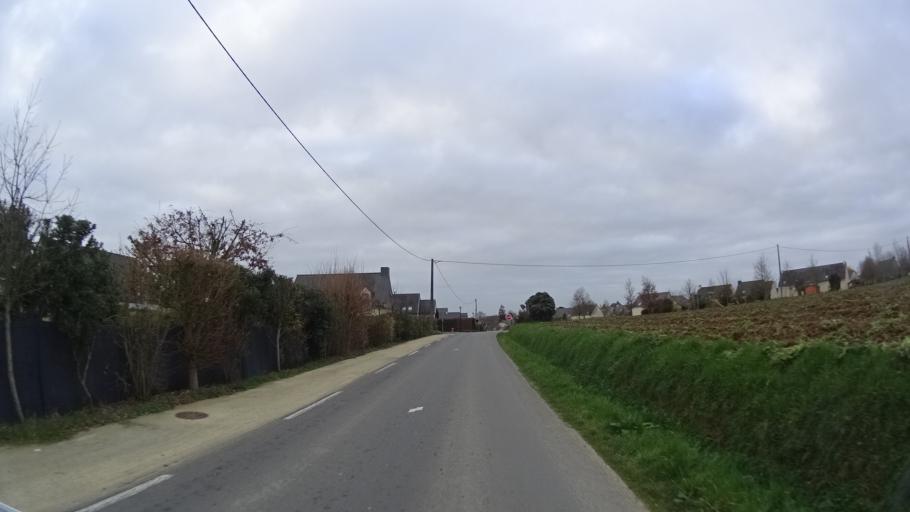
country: FR
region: Brittany
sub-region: Departement d'Ille-et-Vilaine
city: Saint-Gilles
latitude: 48.1951
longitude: -1.8322
